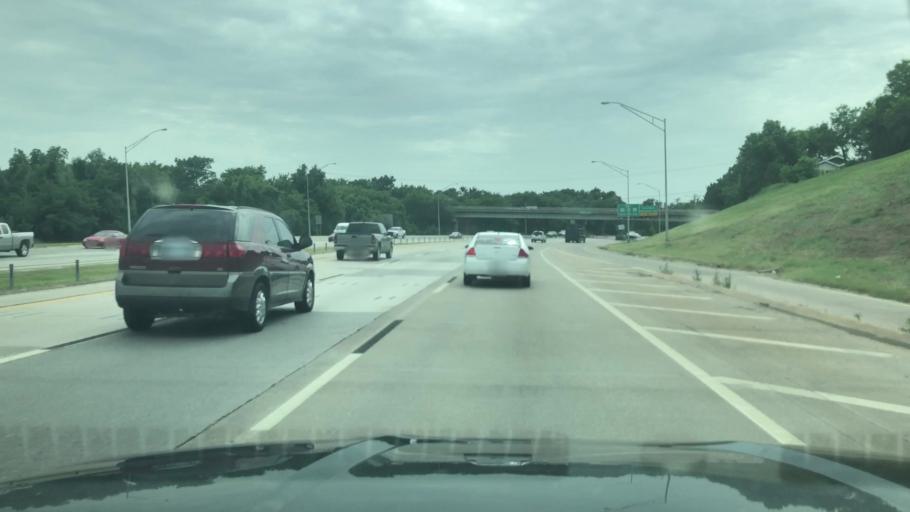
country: US
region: Oklahoma
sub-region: Tulsa County
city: Tulsa
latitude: 36.1561
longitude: -96.0092
